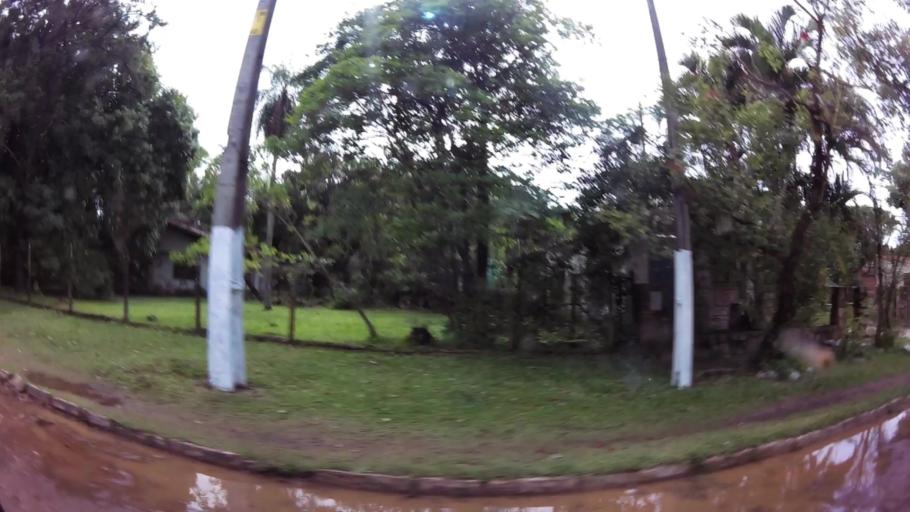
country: PY
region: Central
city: Limpio
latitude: -25.1396
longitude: -57.4725
